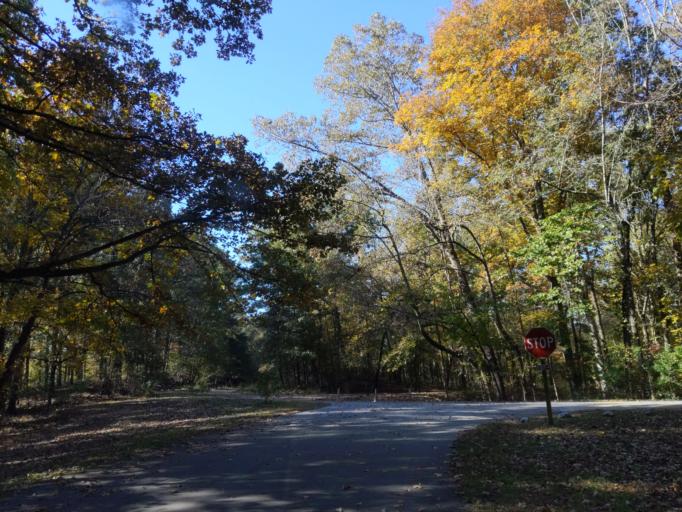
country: US
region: Georgia
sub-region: Franklin County
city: Gumlog
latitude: 34.4933
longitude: -83.0736
